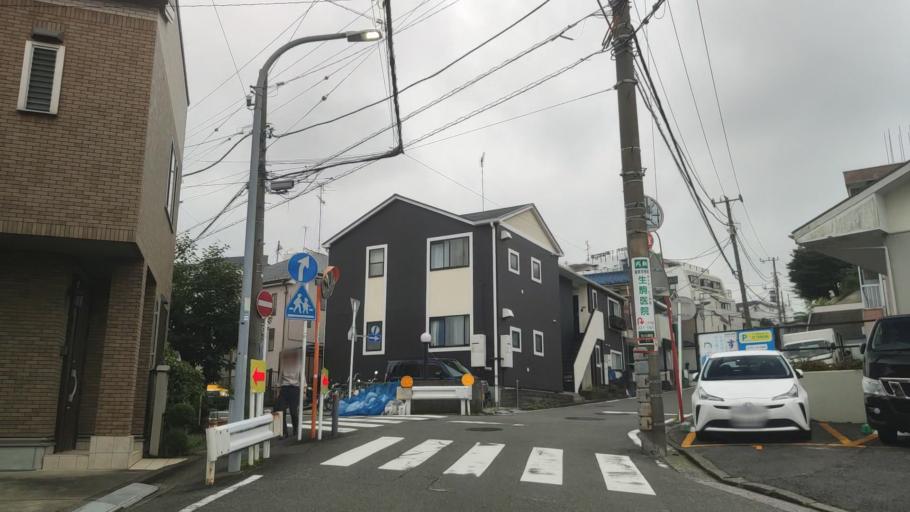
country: JP
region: Kanagawa
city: Yokohama
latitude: 35.4452
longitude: 139.6052
